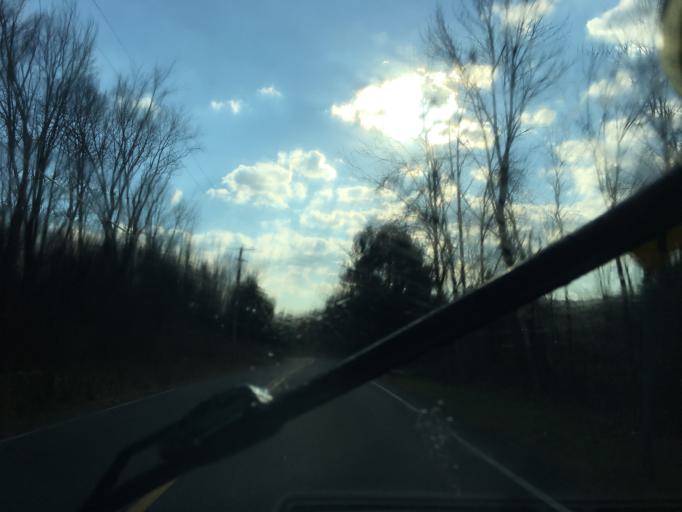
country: US
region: New York
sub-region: Rensselaer County
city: East Greenbush
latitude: 42.6333
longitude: -73.6702
